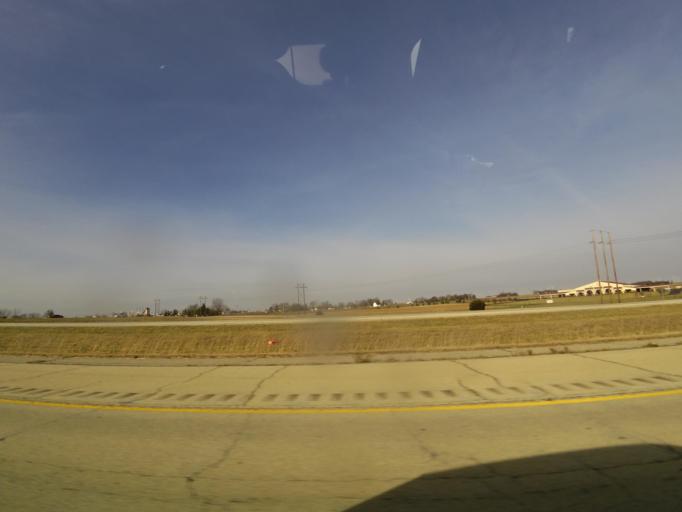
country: US
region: Illinois
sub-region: Macon County
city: Forsyth
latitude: 39.8961
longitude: -89.0045
